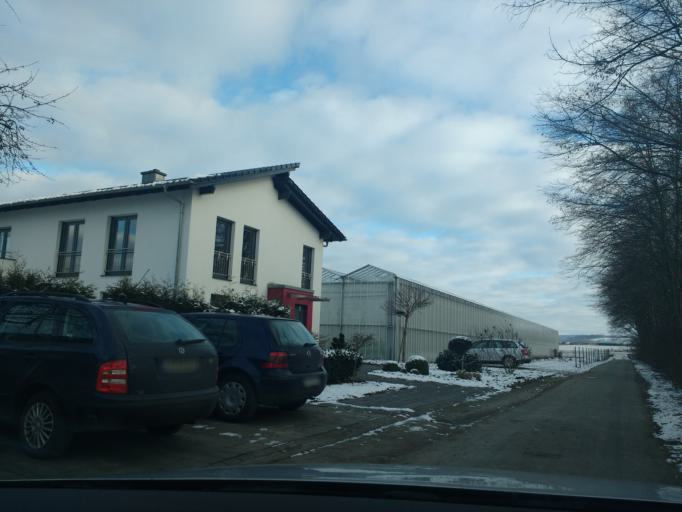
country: DE
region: North Rhine-Westphalia
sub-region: Regierungsbezirk Detmold
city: Paderborn
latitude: 51.7393
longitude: 8.7911
